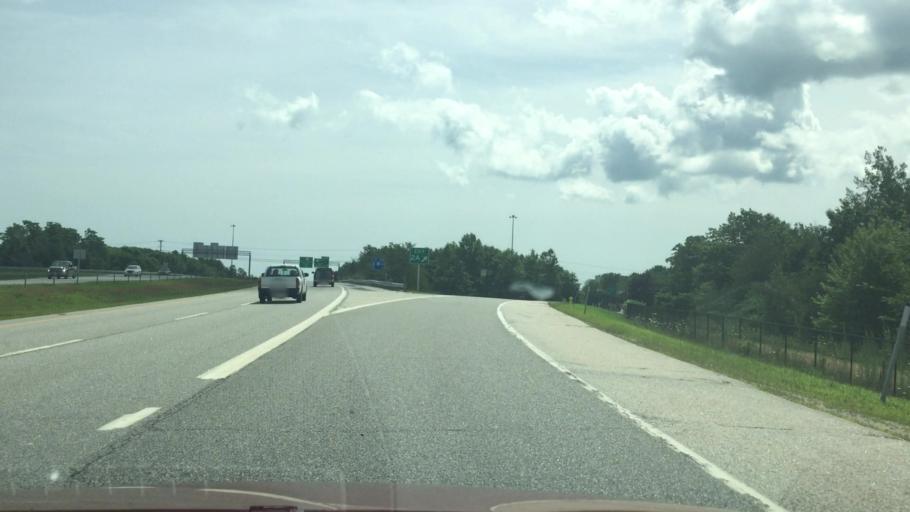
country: US
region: Maine
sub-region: York County
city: Saco
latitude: 43.5129
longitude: -70.4356
